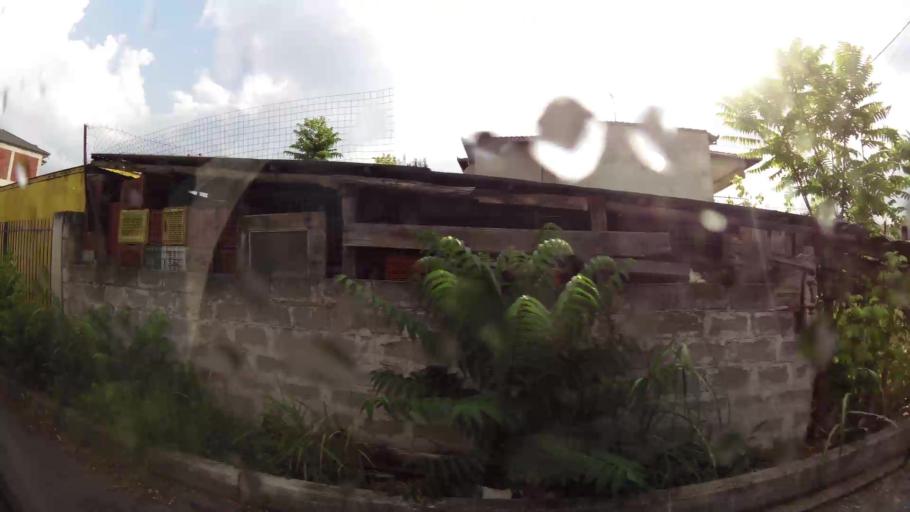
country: GR
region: Central Macedonia
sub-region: Nomos Imathias
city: Veroia
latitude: 40.5408
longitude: 22.2005
